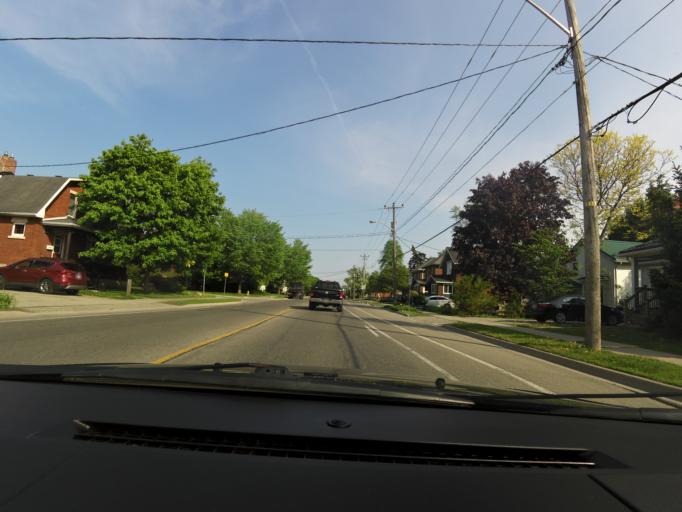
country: CA
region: Ontario
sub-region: Wellington County
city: Guelph
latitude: 43.5576
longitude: -80.2672
